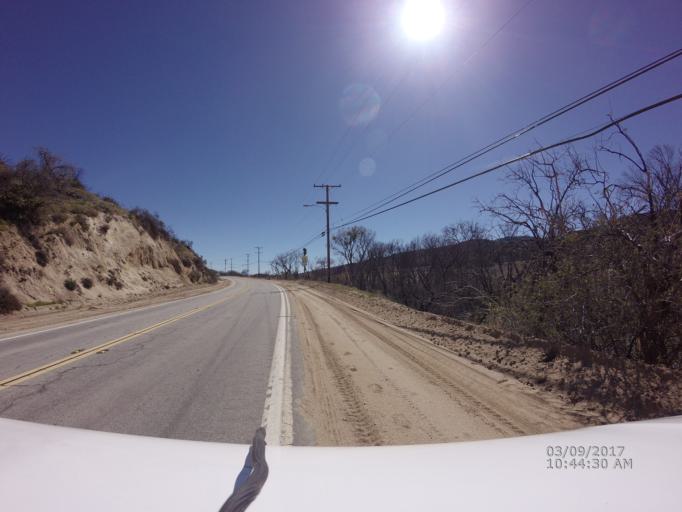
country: US
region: California
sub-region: Los Angeles County
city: Green Valley
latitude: 34.6715
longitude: -118.4267
